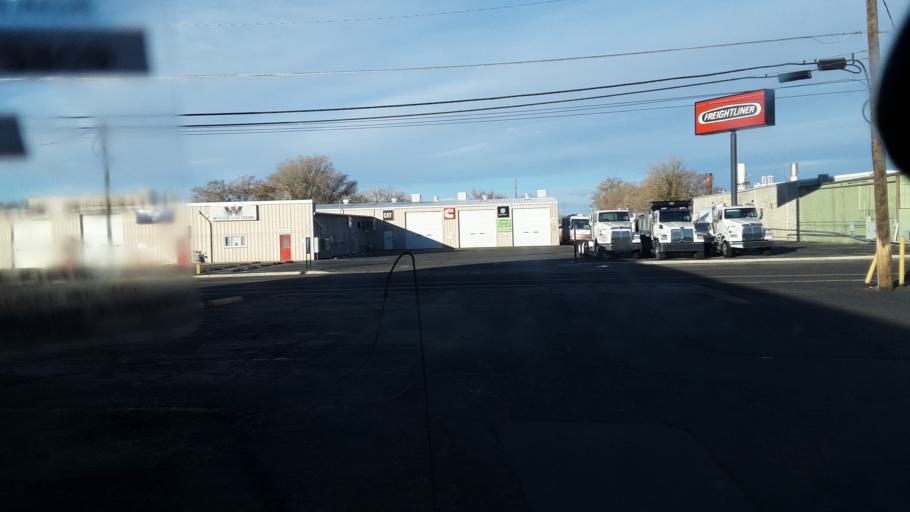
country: US
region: New Mexico
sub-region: San Juan County
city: Farmington
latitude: 36.7240
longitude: -108.1888
